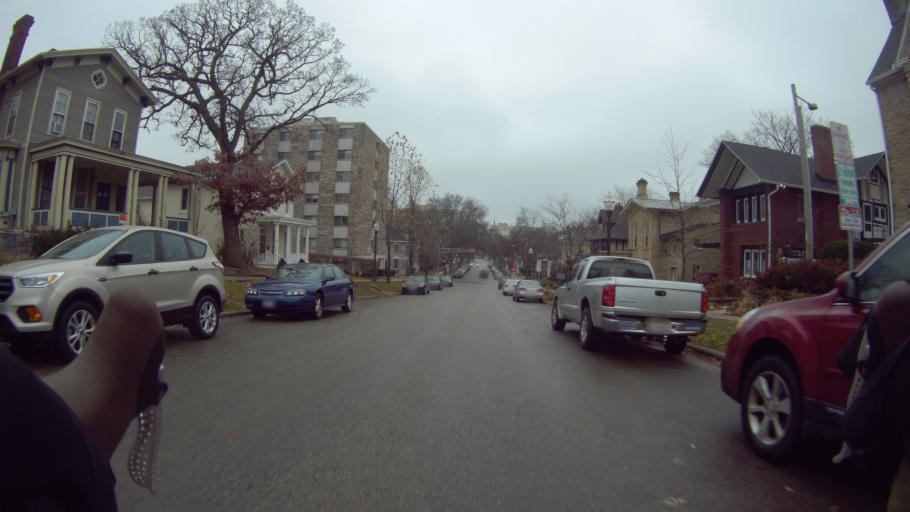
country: US
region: Wisconsin
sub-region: Dane County
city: Madison
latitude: 43.0779
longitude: -89.3907
